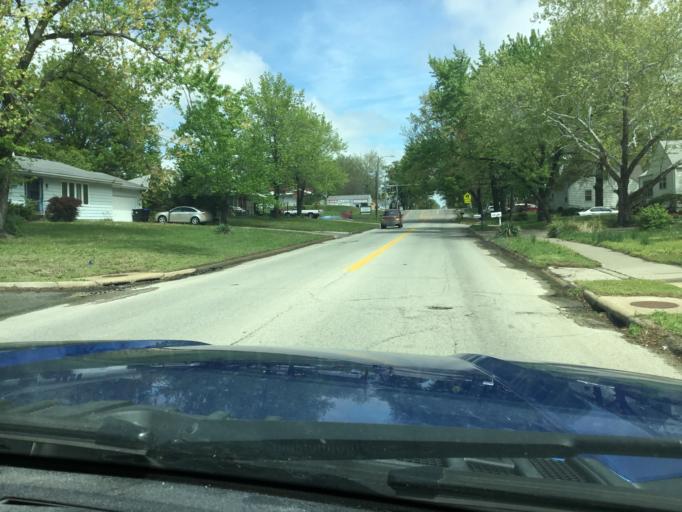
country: US
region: Kansas
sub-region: Shawnee County
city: Topeka
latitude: 39.0137
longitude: -95.6609
